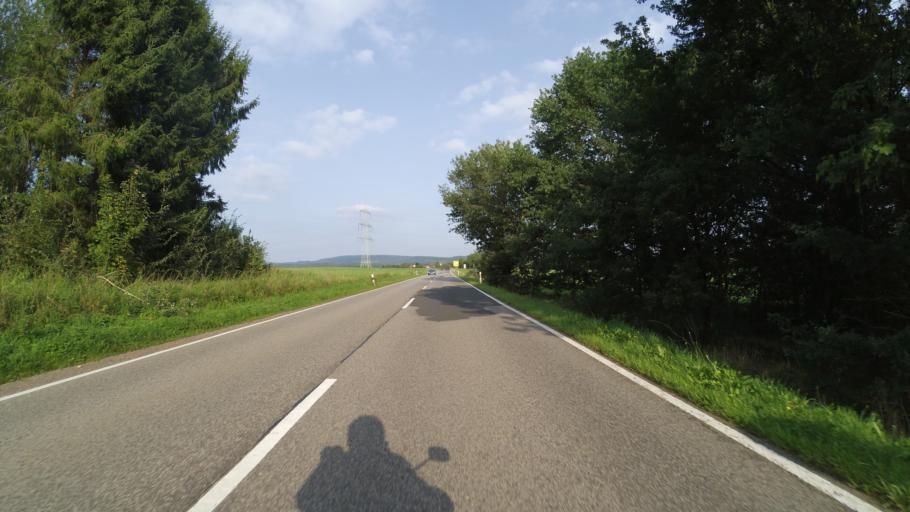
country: DE
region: Saarland
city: Wadern
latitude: 49.5396
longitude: 6.8680
